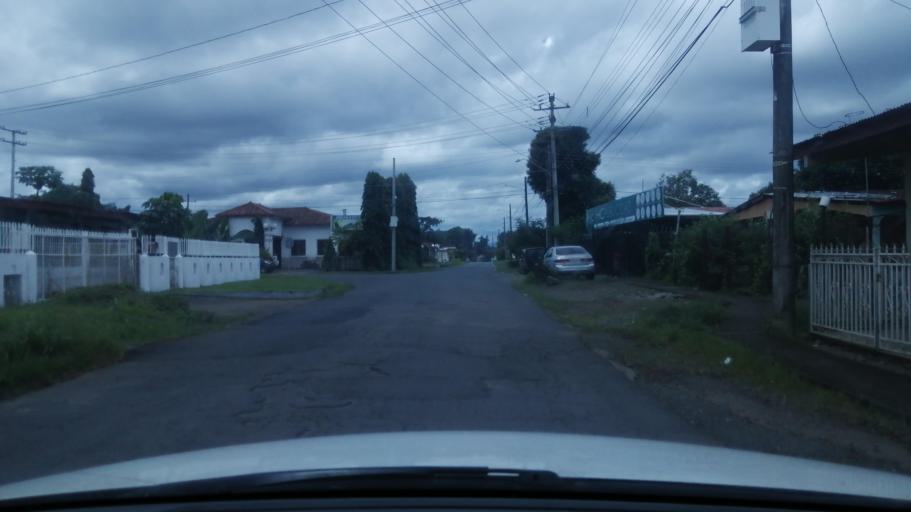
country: PA
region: Chiriqui
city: David
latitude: 8.4296
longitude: -82.4195
